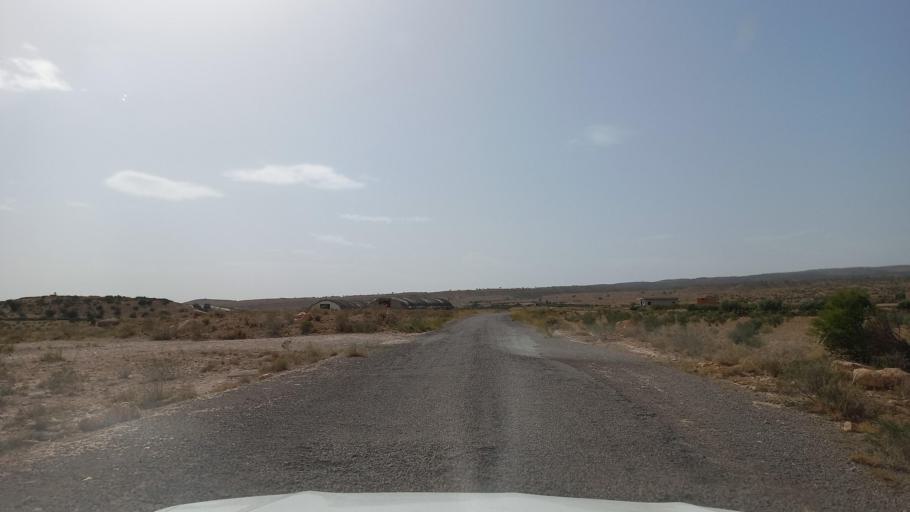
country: TN
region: Al Qasrayn
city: Kasserine
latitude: 35.3028
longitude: 8.9462
